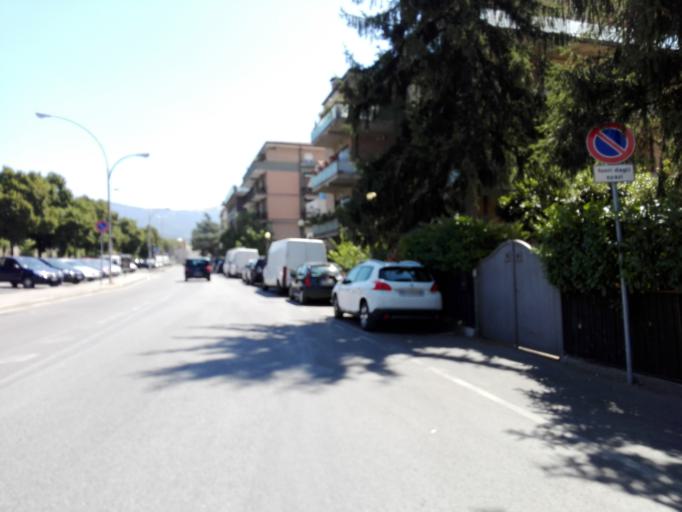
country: IT
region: Umbria
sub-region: Provincia di Perugia
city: Foligno
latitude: 42.9523
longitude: 12.6987
